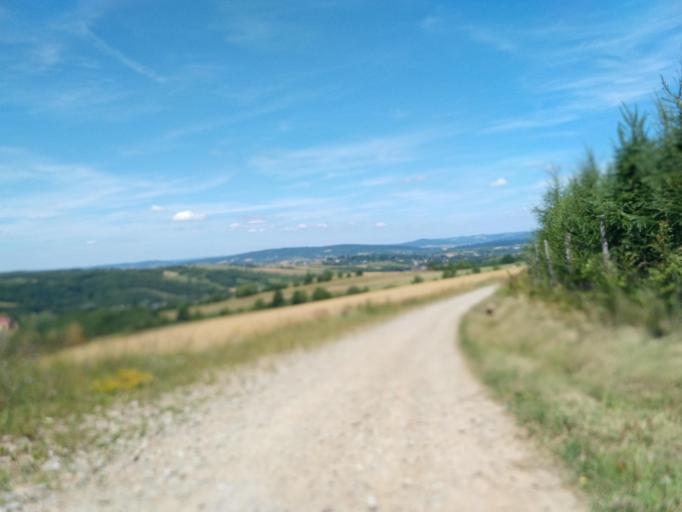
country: PL
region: Subcarpathian Voivodeship
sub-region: Powiat sanocki
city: Bukowsko
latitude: 49.4998
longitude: 22.0949
